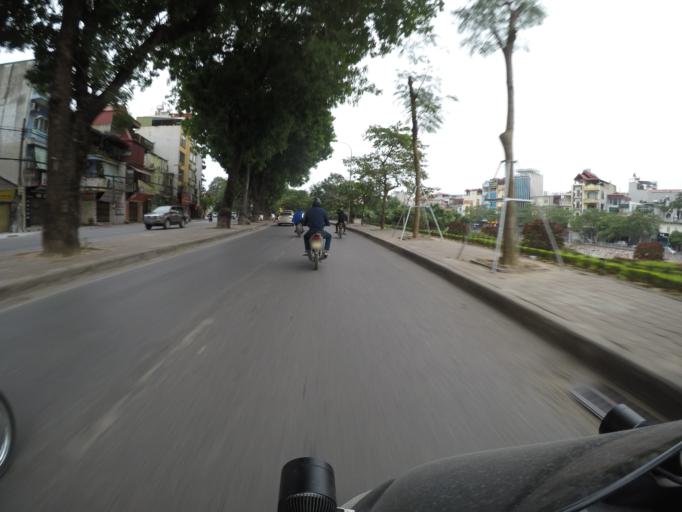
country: VN
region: Ha Noi
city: Cau Giay
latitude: 21.0253
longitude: 105.7981
